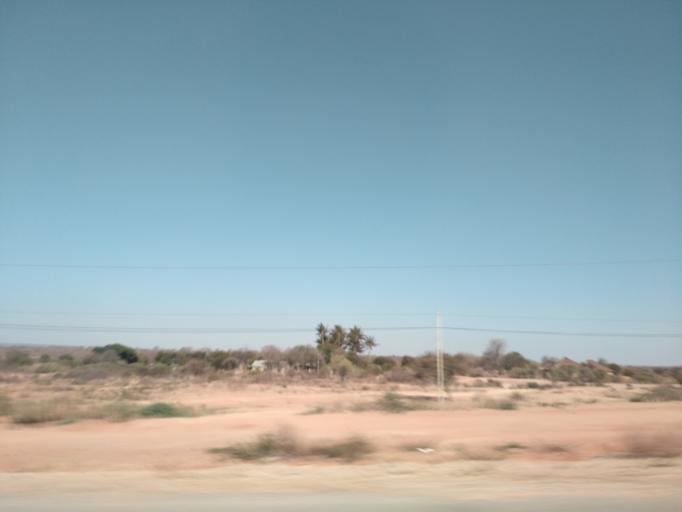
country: TZ
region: Dodoma
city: Dodoma
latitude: -6.0975
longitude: 35.7490
